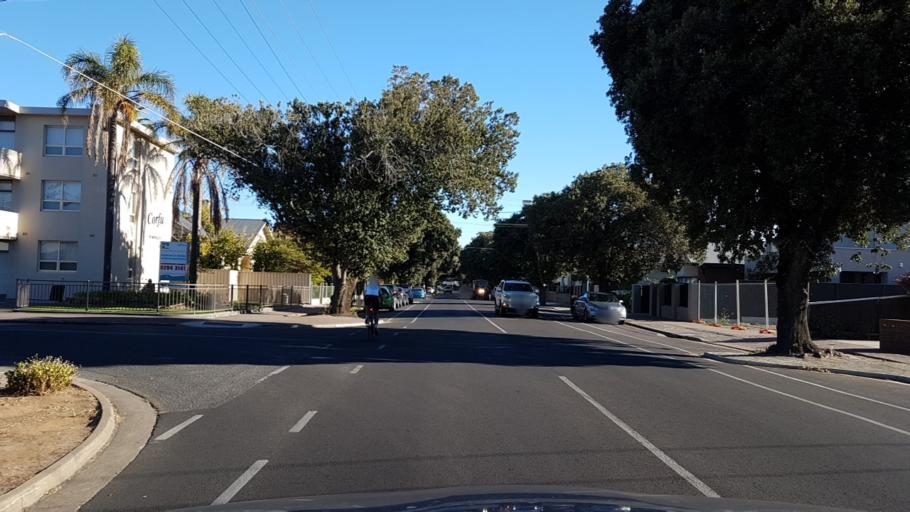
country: AU
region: South Australia
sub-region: Adelaide
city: Glenelg
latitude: -34.9839
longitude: 138.5133
